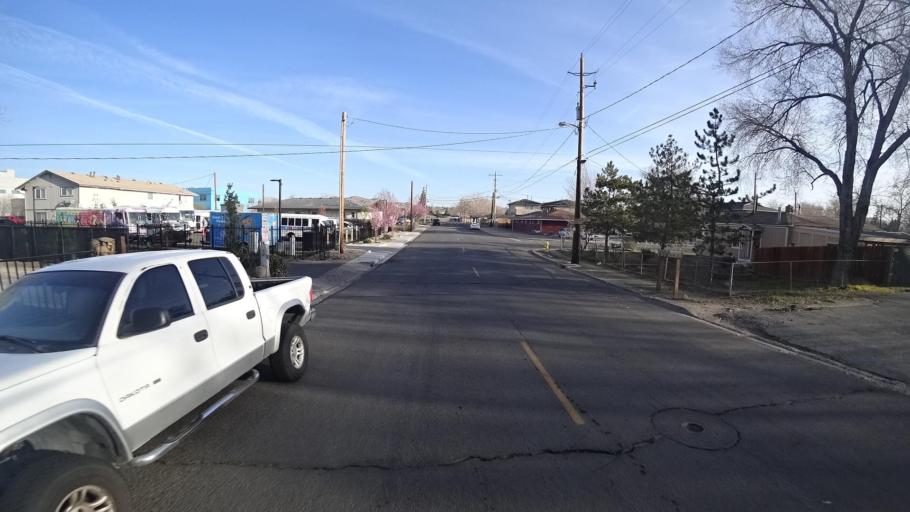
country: US
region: Nevada
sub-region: Washoe County
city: Sparks
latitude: 39.5375
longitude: -119.7796
